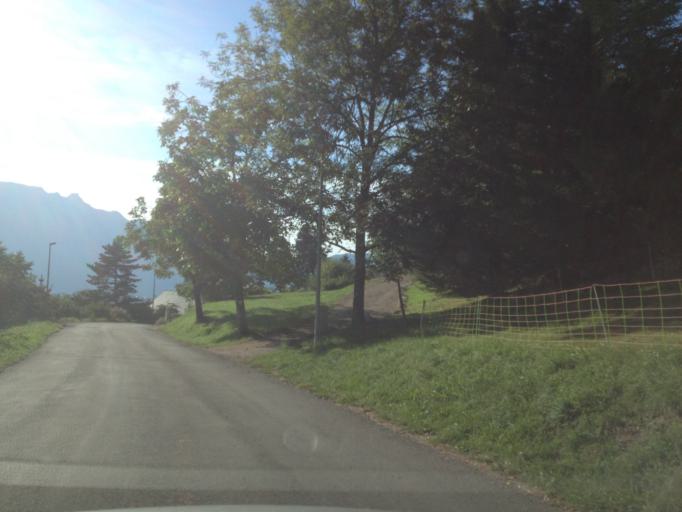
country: FR
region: Rhone-Alpes
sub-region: Departement de la Savoie
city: Mery
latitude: 45.6631
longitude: 5.9425
